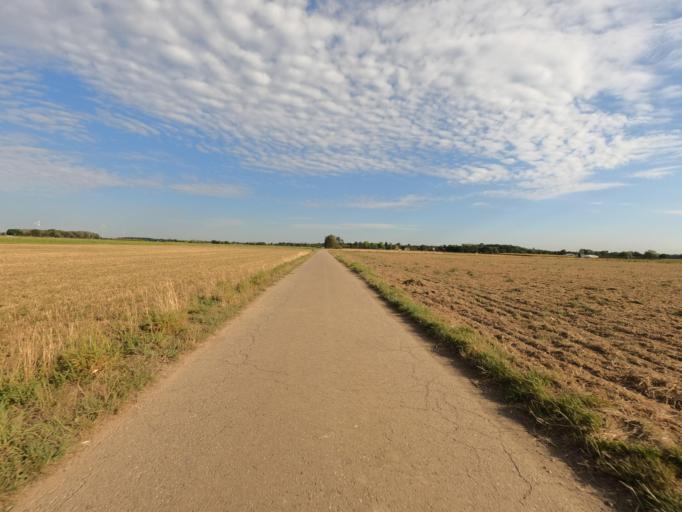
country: DE
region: North Rhine-Westphalia
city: Wegberg
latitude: 51.1024
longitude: 6.2592
